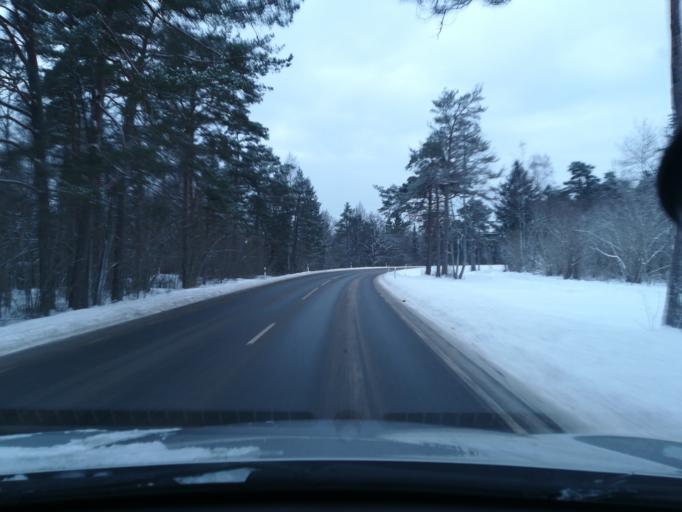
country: EE
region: Harju
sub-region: Paldiski linn
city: Paldiski
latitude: 59.3940
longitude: 24.2422
